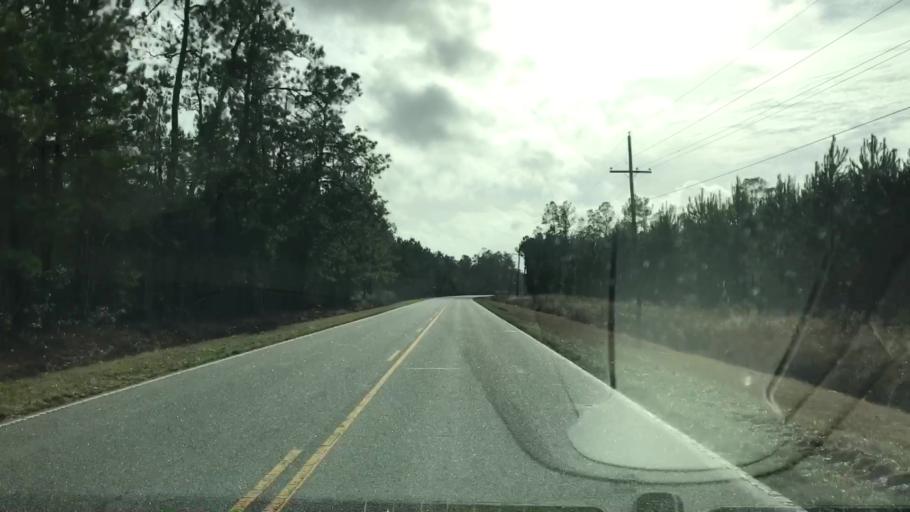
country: US
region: South Carolina
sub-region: Williamsburg County
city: Andrews
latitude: 33.4091
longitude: -79.6088
